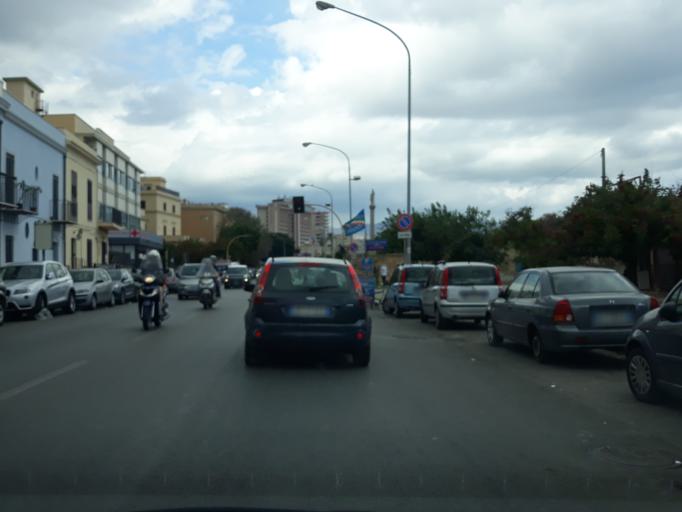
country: IT
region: Sicily
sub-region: Palermo
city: Ciaculli
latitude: 38.1061
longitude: 13.3870
